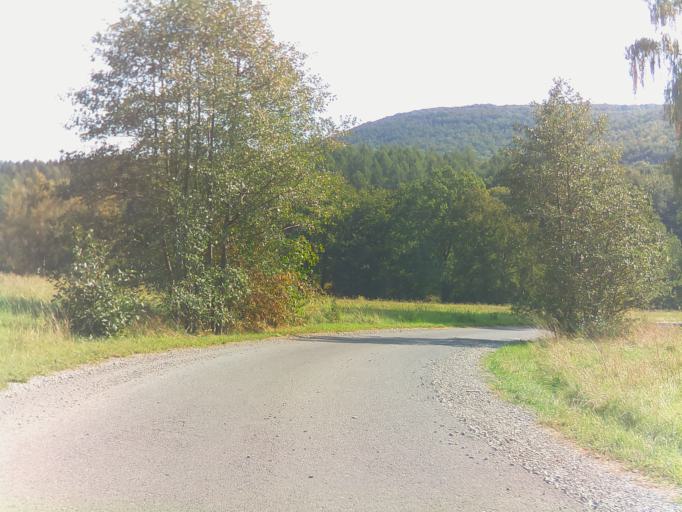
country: DE
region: Thuringia
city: Christes
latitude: 50.6436
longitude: 10.4654
